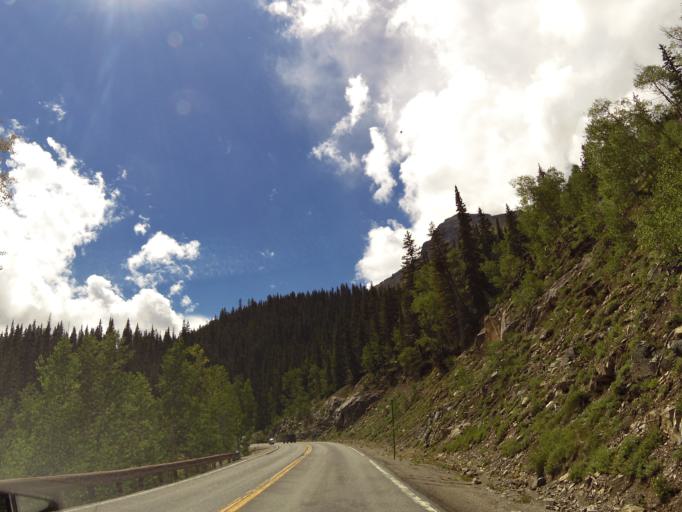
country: US
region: Colorado
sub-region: San Juan County
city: Silverton
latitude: 37.7860
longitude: -107.6721
